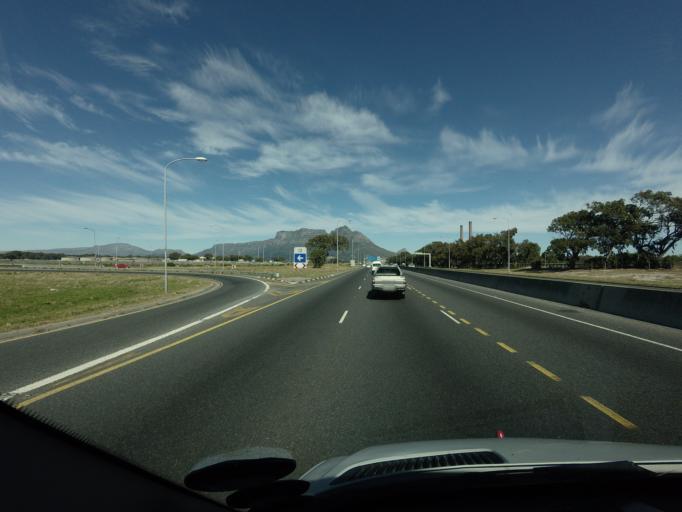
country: ZA
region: Western Cape
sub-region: City of Cape Town
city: Lansdowne
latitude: -33.9503
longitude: 18.5214
